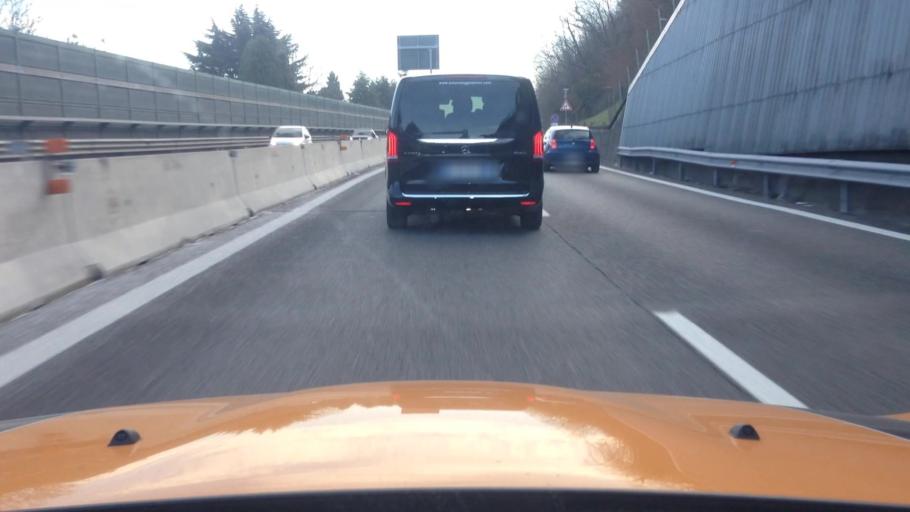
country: IT
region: Lombardy
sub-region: Provincia di Como
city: San Fermo della Battaglia
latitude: 45.8218
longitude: 9.0521
